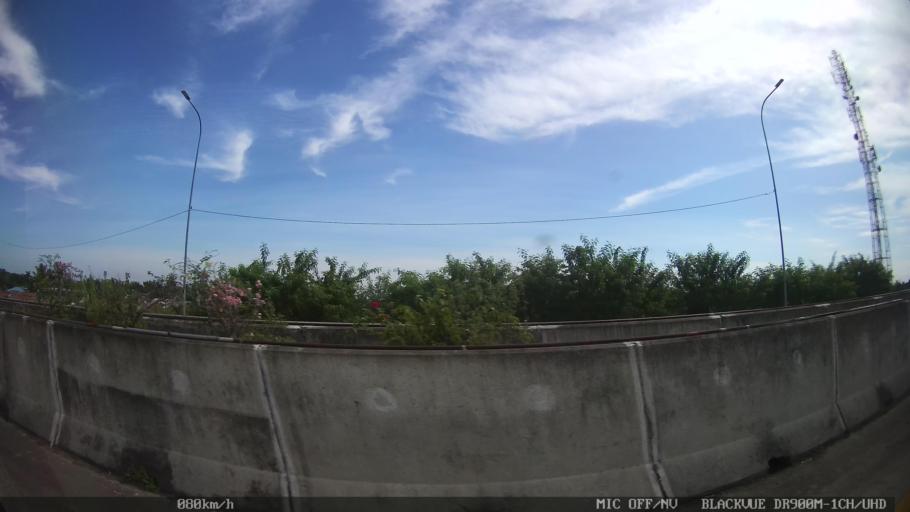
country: ID
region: North Sumatra
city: Binjai
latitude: 3.6458
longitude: 98.5523
